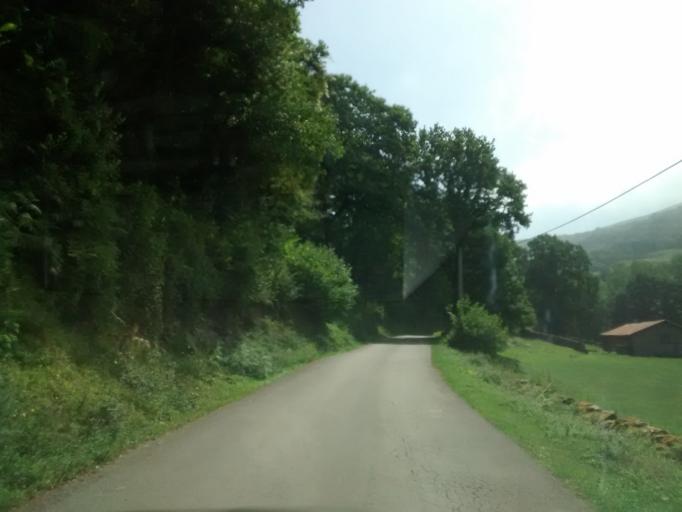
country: ES
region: Cantabria
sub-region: Provincia de Cantabria
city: Ruente
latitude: 43.2432
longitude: -4.2367
